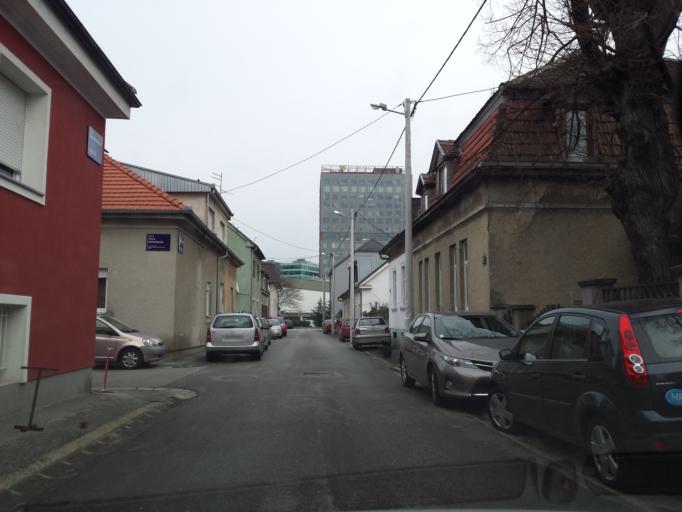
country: HR
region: Grad Zagreb
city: Zagreb - Centar
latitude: 45.8019
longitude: 15.9979
